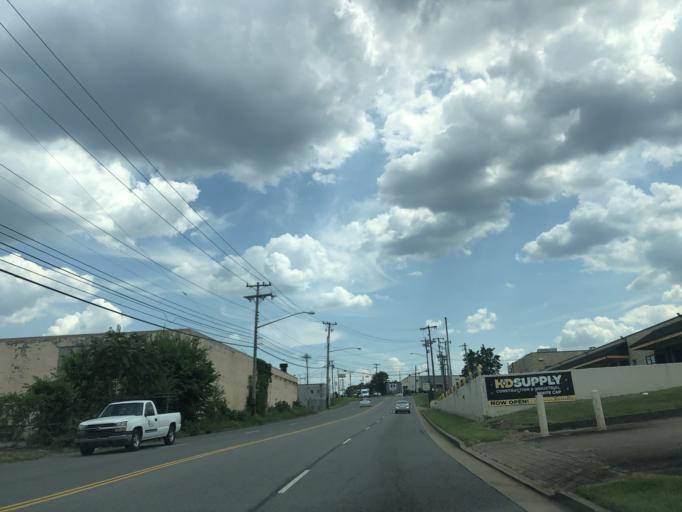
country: US
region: Tennessee
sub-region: Davidson County
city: Nashville
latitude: 36.1366
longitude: -86.7468
